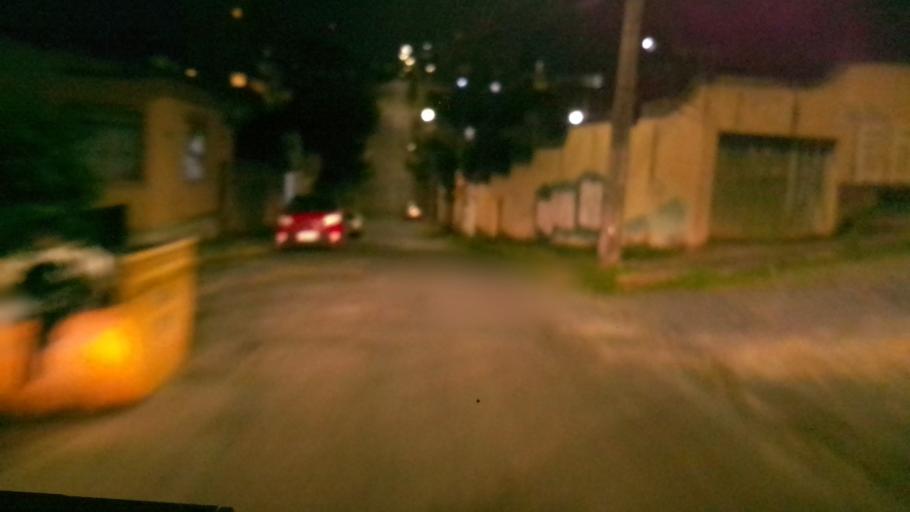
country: BR
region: Minas Gerais
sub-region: Belo Horizonte
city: Belo Horizonte
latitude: -19.9171
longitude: -43.9184
